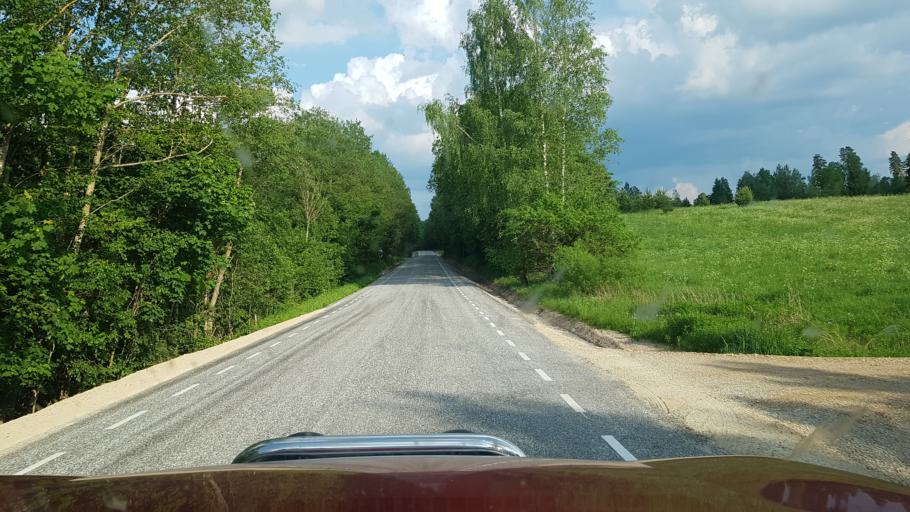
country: EE
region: Tartu
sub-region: UElenurme vald
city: Ulenurme
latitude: 58.1064
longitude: 26.7653
